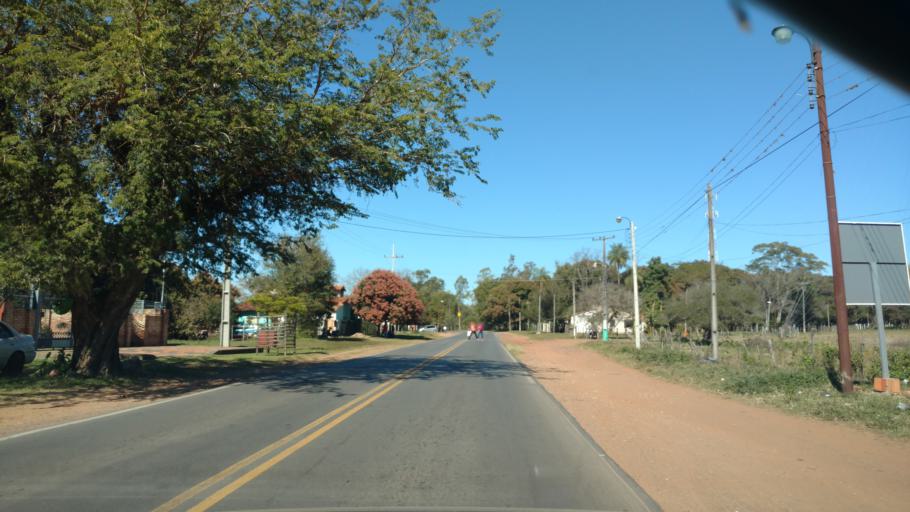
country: PY
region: Central
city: Ypacarai
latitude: -25.4521
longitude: -57.2730
